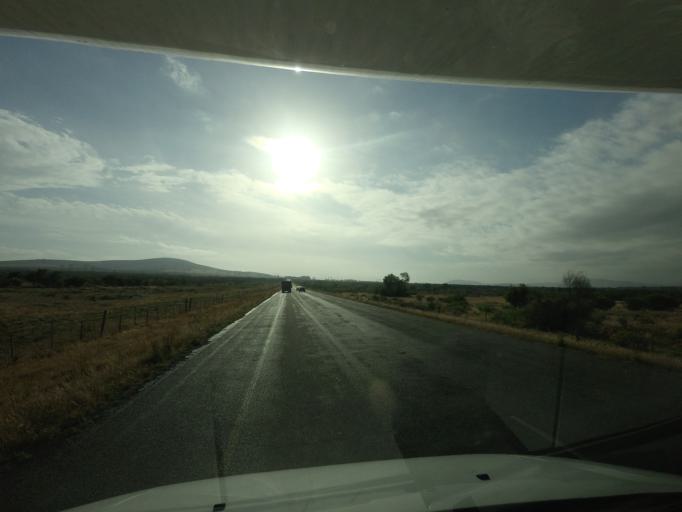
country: ZA
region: Western Cape
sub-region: City of Cape Town
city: Sunset Beach
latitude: -33.7246
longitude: 18.5243
